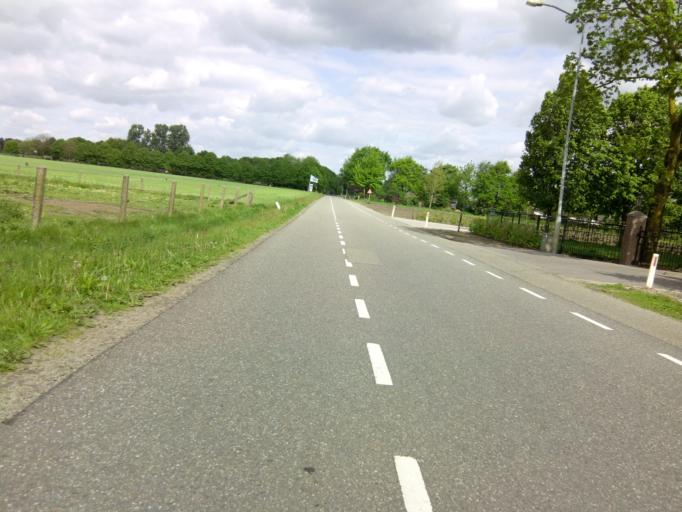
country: NL
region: Gelderland
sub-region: Gemeente Ede
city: Ede
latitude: 52.0749
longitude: 5.6770
